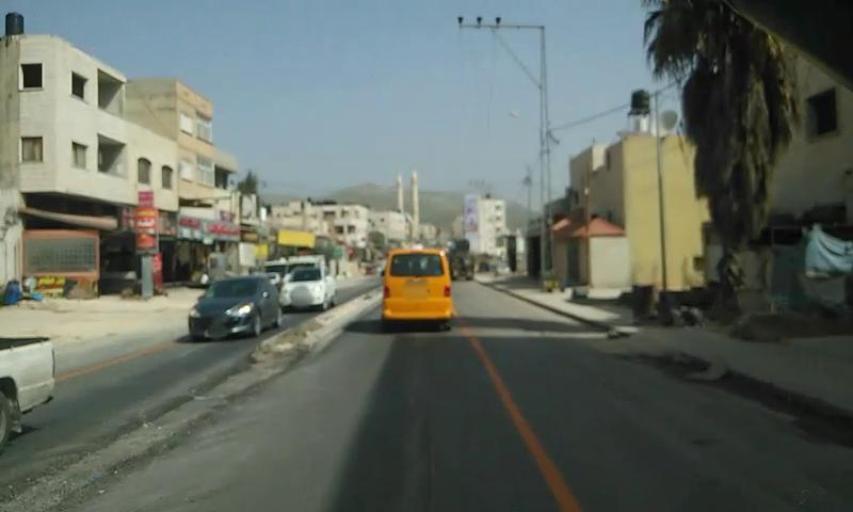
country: PS
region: West Bank
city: Huwwarah
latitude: 32.1540
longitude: 35.2592
